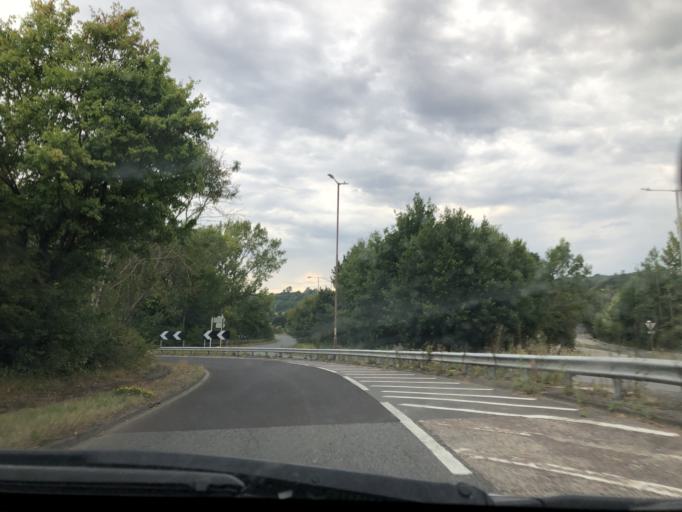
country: GB
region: England
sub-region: Kent
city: Sevenoaks
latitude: 51.2399
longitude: 0.2104
